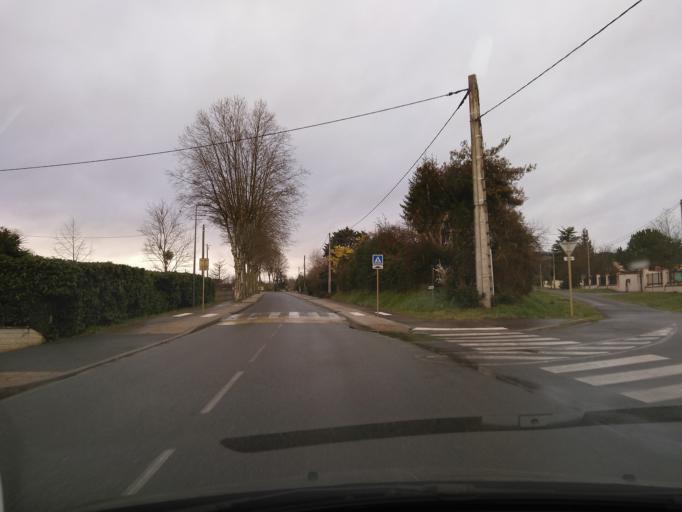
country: FR
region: Midi-Pyrenees
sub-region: Departement de la Haute-Garonne
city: Montesquieu-Volvestre
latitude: 43.2162
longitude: 1.2211
